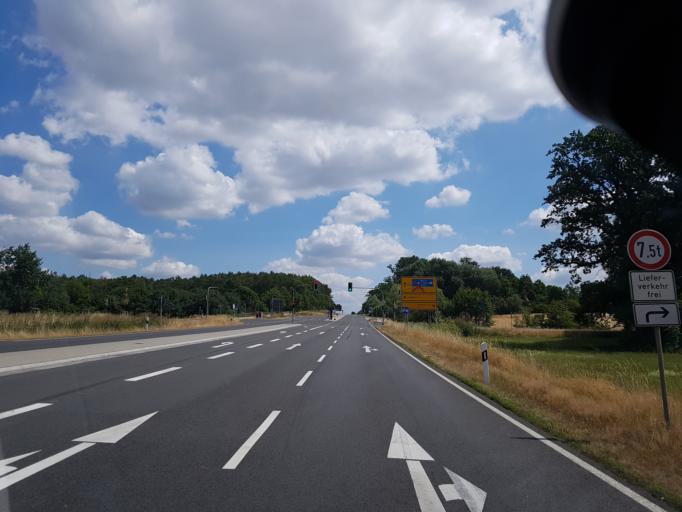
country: DE
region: Brandenburg
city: Drebkau
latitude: 51.6913
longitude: 14.2671
